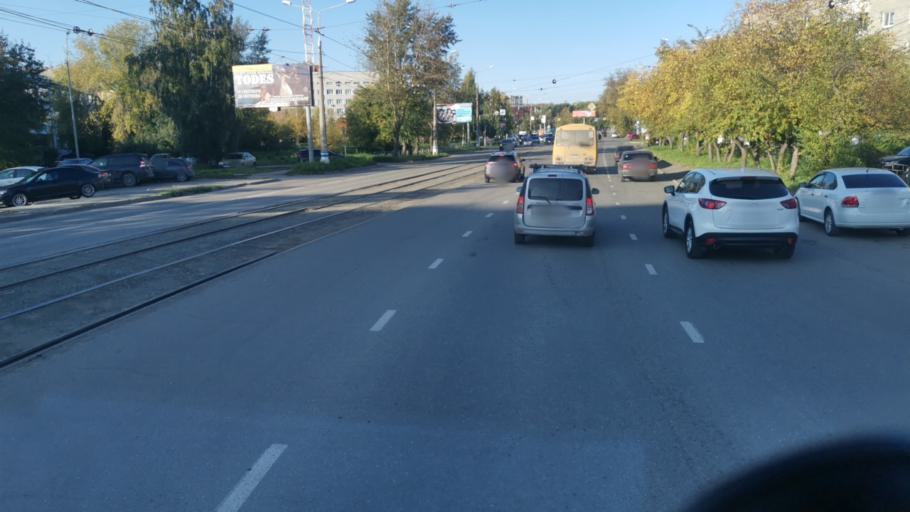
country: RU
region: Sverdlovsk
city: Nizhniy Tagil
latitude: 57.9095
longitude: 59.9470
